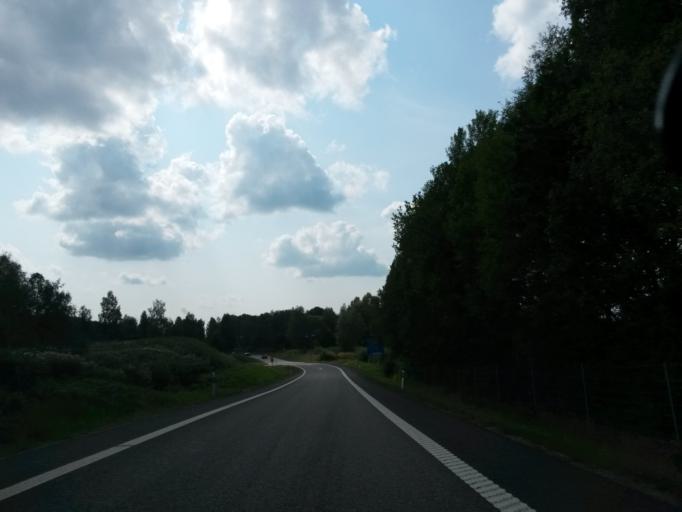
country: SE
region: Vaestra Goetaland
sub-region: Lerums Kommun
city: Lerum
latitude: 57.7748
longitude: 12.2939
